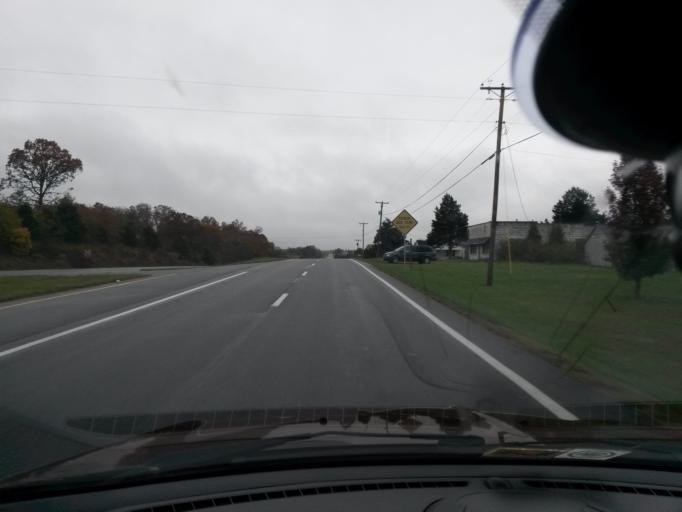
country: US
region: Virginia
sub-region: Botetourt County
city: Fincastle
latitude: 37.5304
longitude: -79.8710
